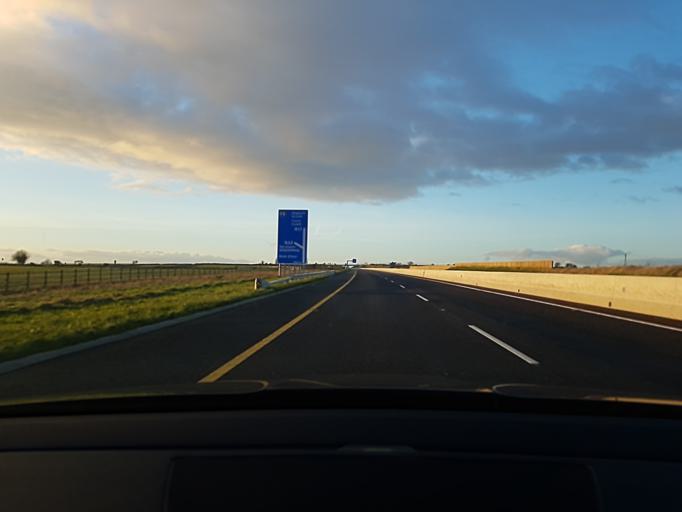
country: IE
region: Connaught
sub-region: County Galway
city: Athenry
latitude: 53.3959
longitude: -8.8067
